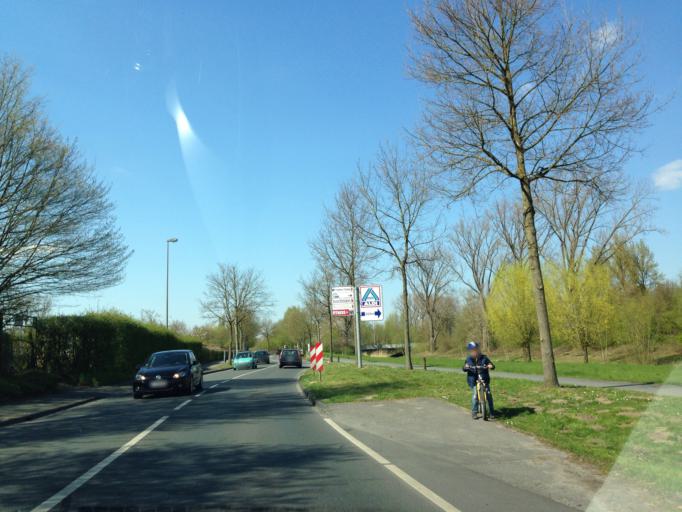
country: DE
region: North Rhine-Westphalia
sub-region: Regierungsbezirk Munster
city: Muenster
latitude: 51.9814
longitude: 7.6314
